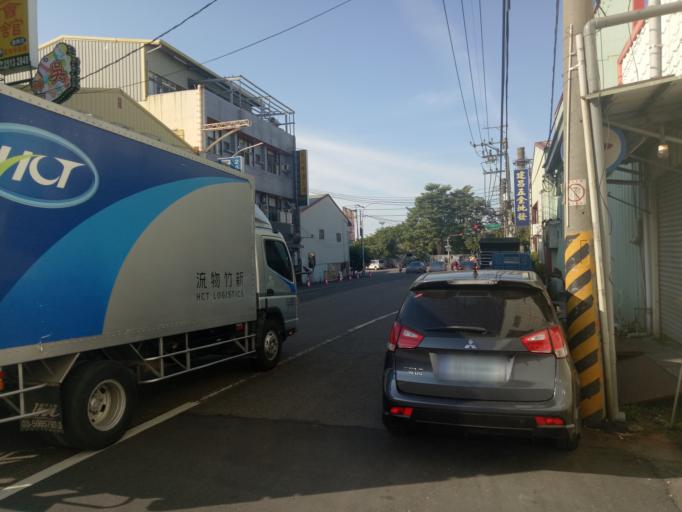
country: TW
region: Taiwan
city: Fengyuan
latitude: 24.2583
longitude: 120.7331
